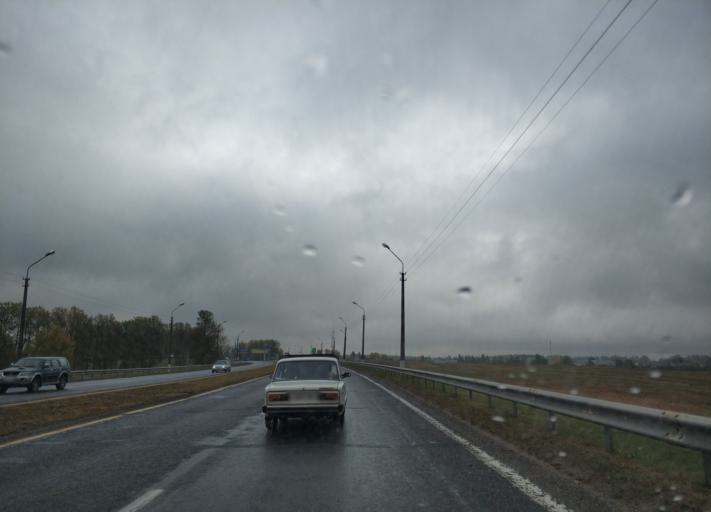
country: BY
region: Vitebsk
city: Vitebsk
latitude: 55.1925
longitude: 30.1317
